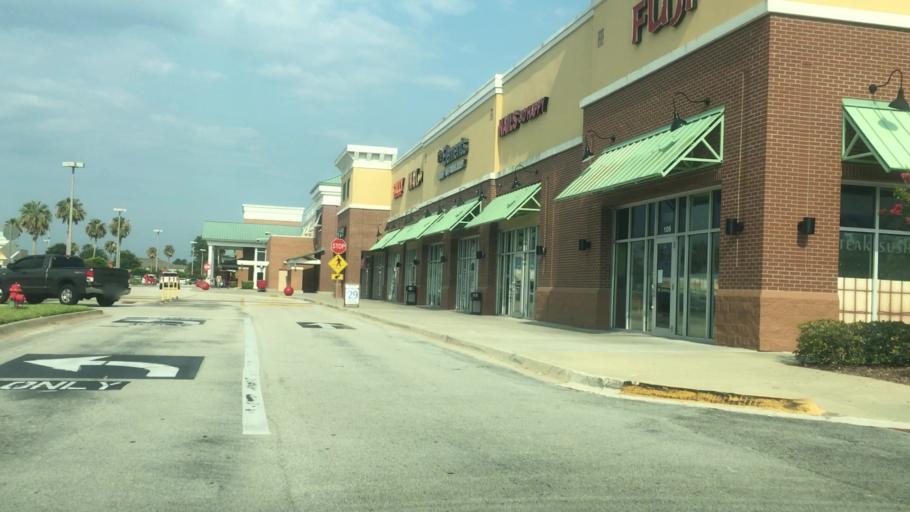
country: US
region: Florida
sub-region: Duval County
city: Jacksonville Beach
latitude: 30.2852
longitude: -81.4582
